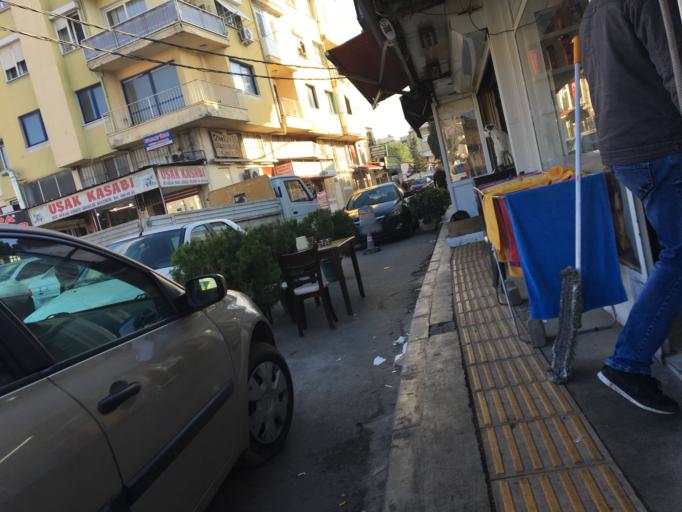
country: TR
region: Izmir
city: Buca
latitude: 38.3881
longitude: 27.1737
